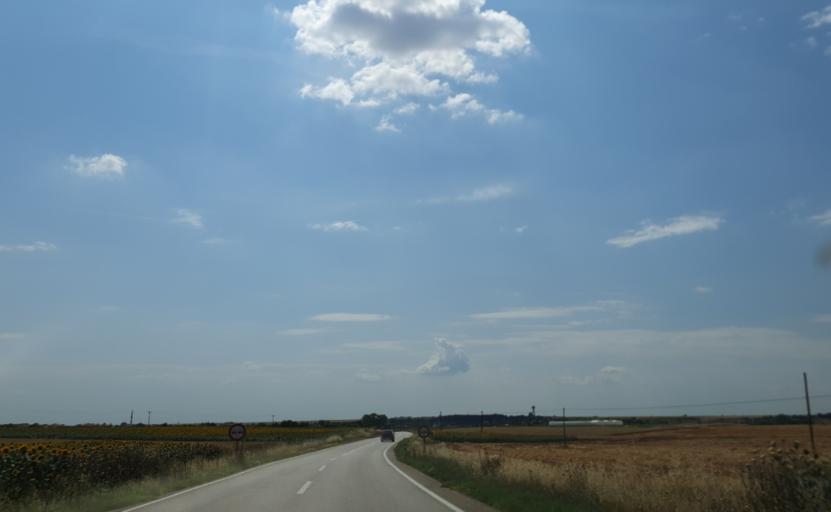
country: TR
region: Tekirdag
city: Beyazkoy
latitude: 41.4450
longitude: 27.5996
